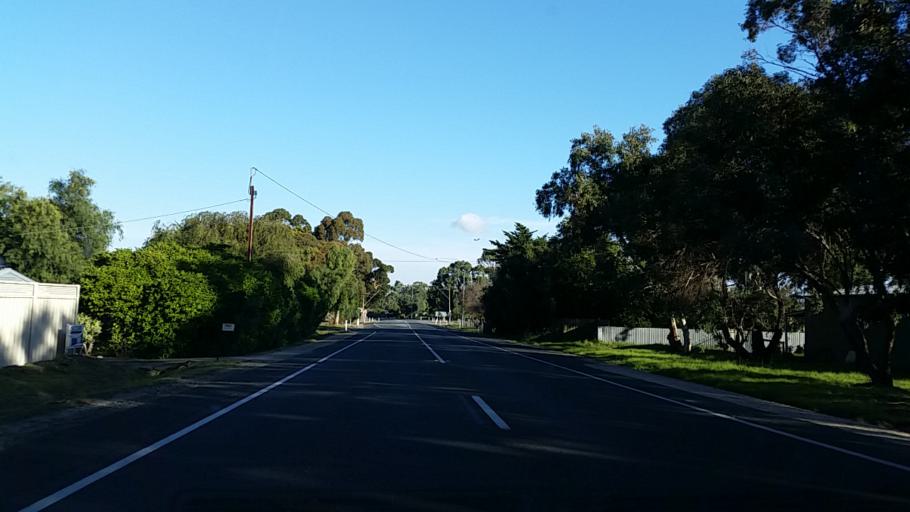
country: AU
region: South Australia
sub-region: Alexandrina
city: Strathalbyn
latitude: -35.2409
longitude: 138.8941
